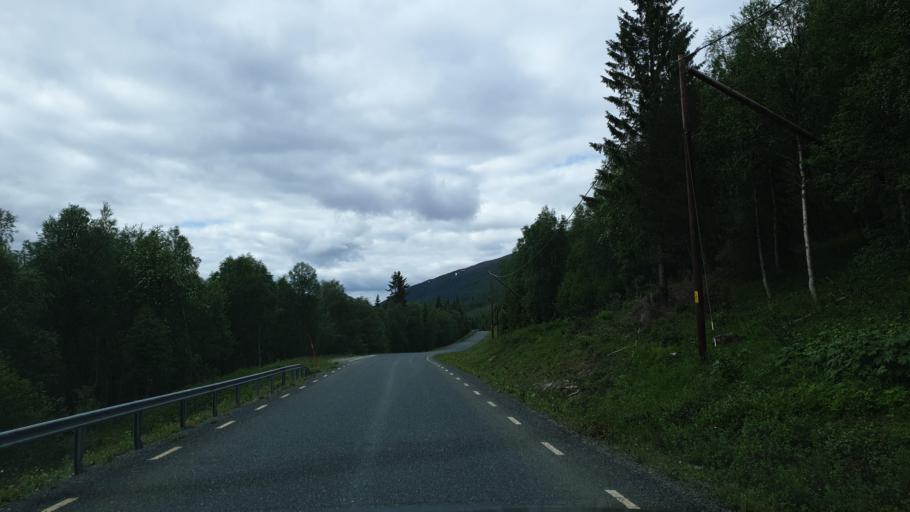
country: NO
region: Nordland
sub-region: Hattfjelldal
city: Hattfjelldal
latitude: 65.4325
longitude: 14.5849
